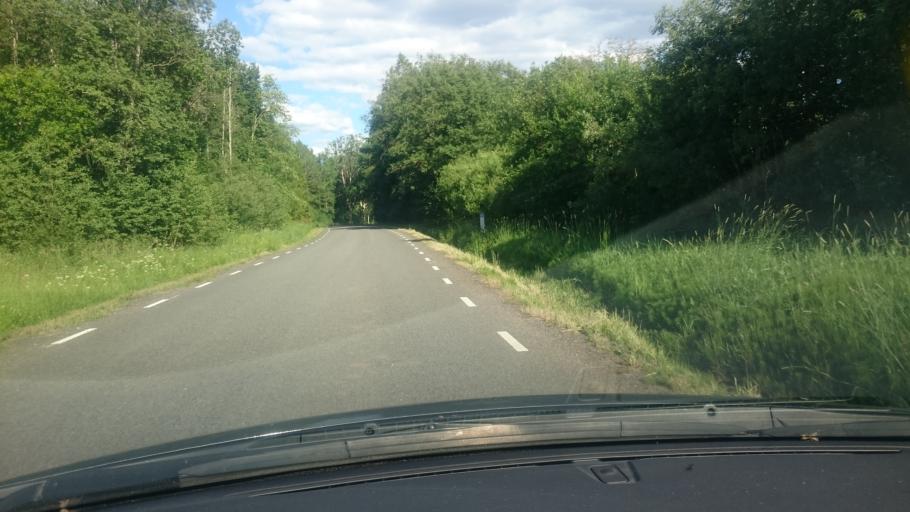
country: EE
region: Harju
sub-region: Rae vald
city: Vaida
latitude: 59.2275
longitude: 24.9553
